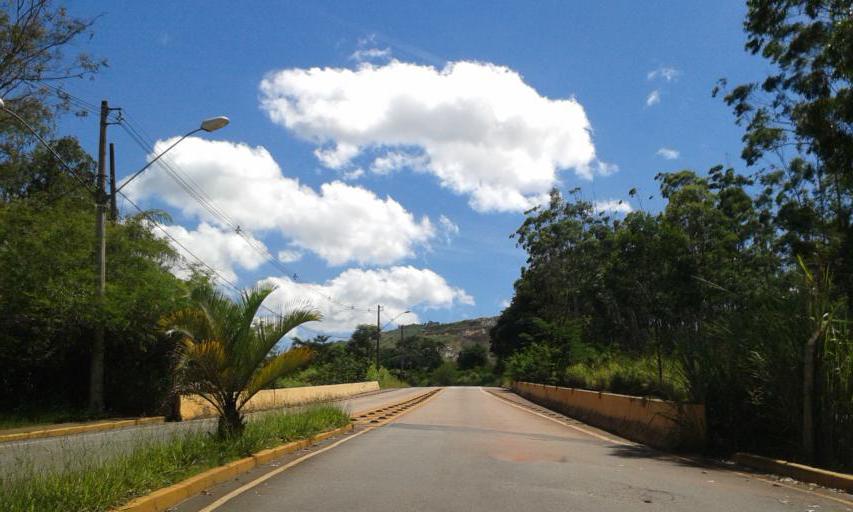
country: BR
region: Minas Gerais
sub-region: Itabira
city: Itabira
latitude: -19.6354
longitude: -43.2405
